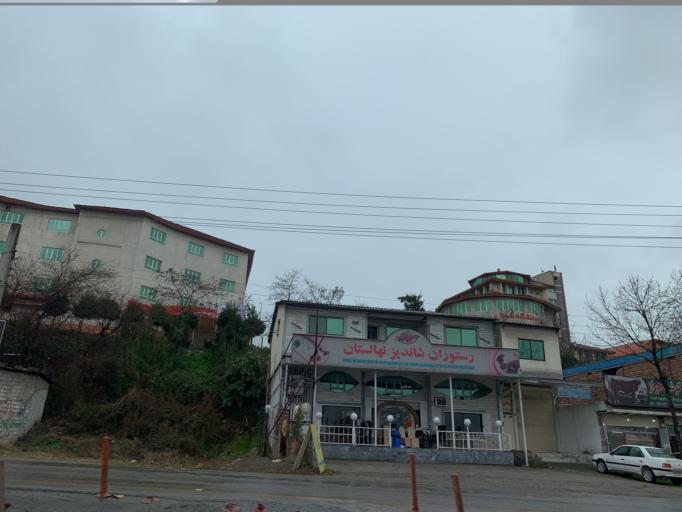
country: IR
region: Mazandaran
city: Amol
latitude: 36.4012
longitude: 52.3465
